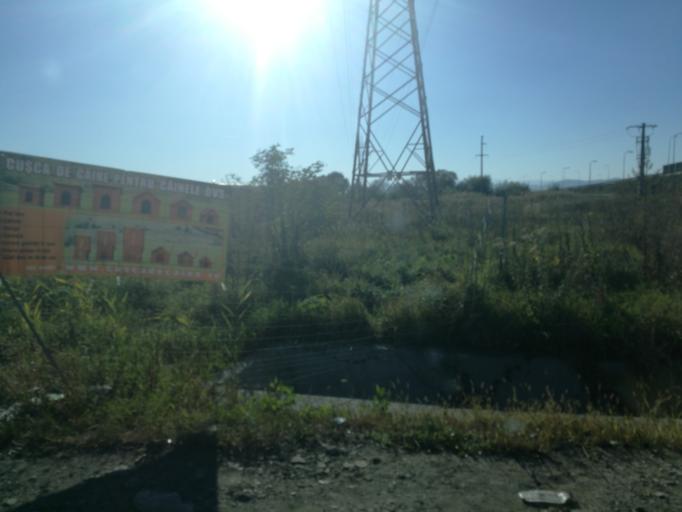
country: RO
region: Brasov
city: Brasov
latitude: 45.6930
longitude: 25.5833
